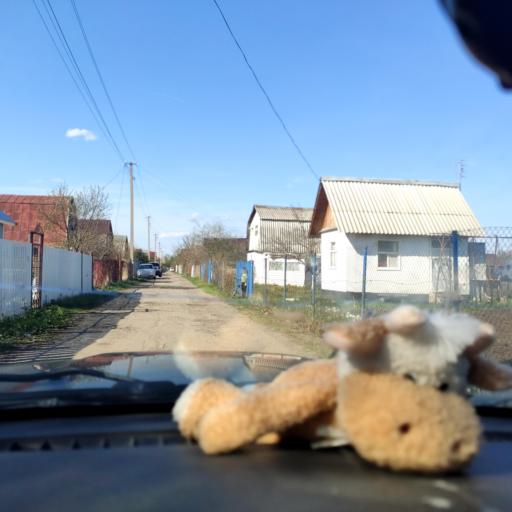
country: RU
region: Samara
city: Tol'yatti
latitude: 53.5988
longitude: 49.2642
